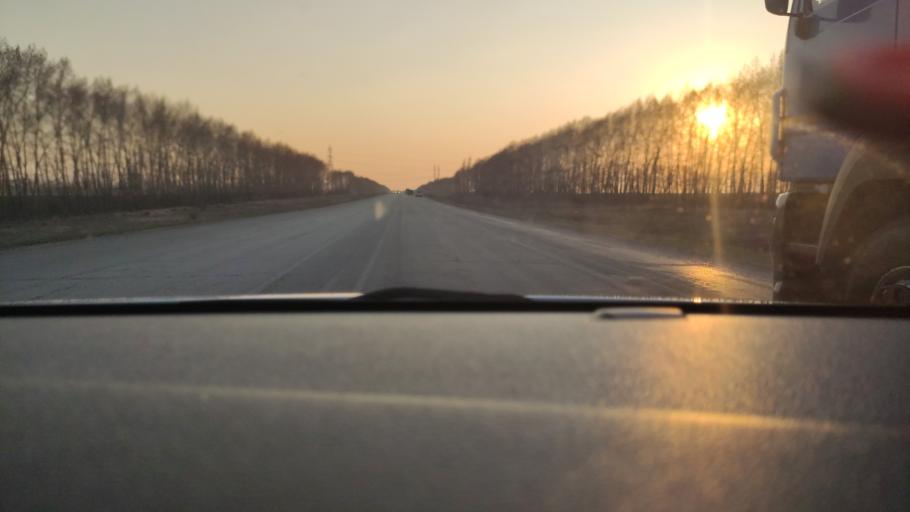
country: RU
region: Voronezj
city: Novovoronezh
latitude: 51.4192
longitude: 39.2839
